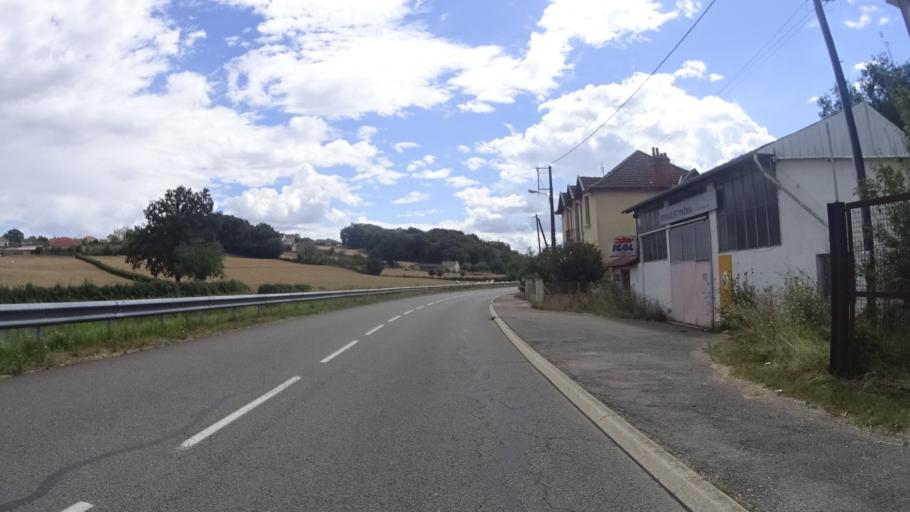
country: FR
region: Bourgogne
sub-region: Departement de Saone-et-Loire
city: Saint-Vallier
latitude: 46.6421
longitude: 4.3335
